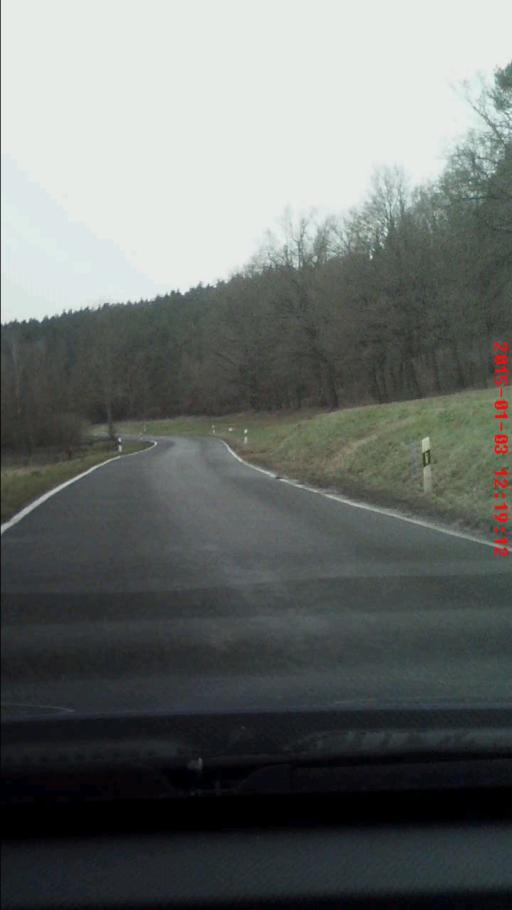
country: DE
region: Thuringia
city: Rittersdorf
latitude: 50.8524
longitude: 11.2664
